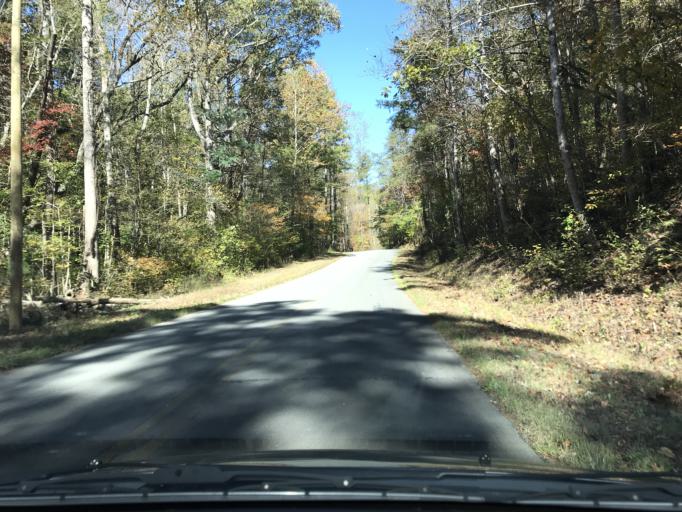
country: US
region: Georgia
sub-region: Dade County
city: Trenton
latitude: 34.9067
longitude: -85.4655
